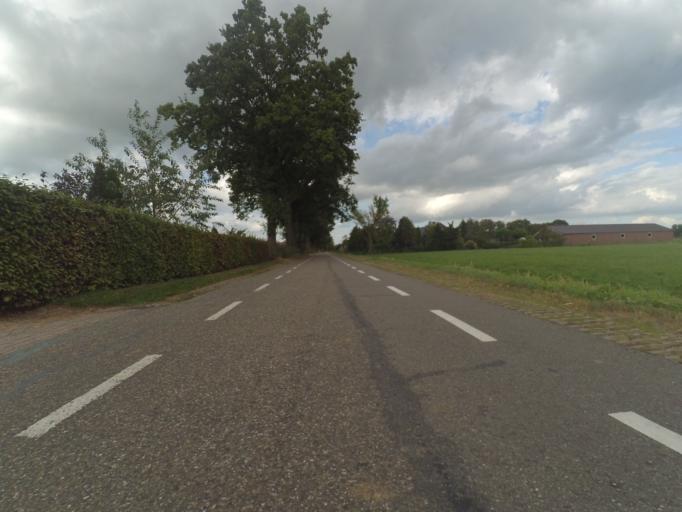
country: NL
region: Utrecht
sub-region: Gemeente Utrechtse Heuvelrug
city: Overberg
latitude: 52.0558
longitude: 5.5210
